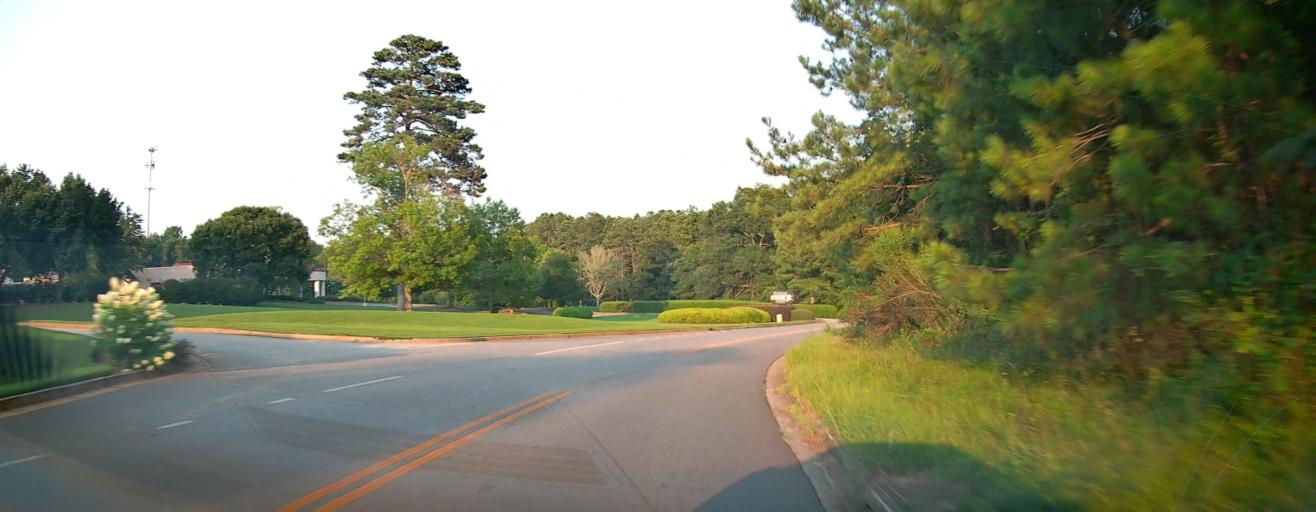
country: US
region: Georgia
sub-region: Bibb County
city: Macon
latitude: 32.9170
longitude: -83.7130
